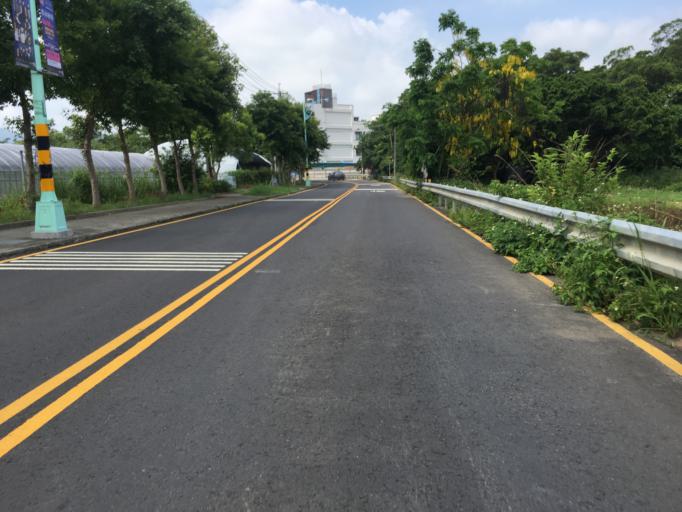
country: TW
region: Taiwan
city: Daxi
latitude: 24.8461
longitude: 121.2427
